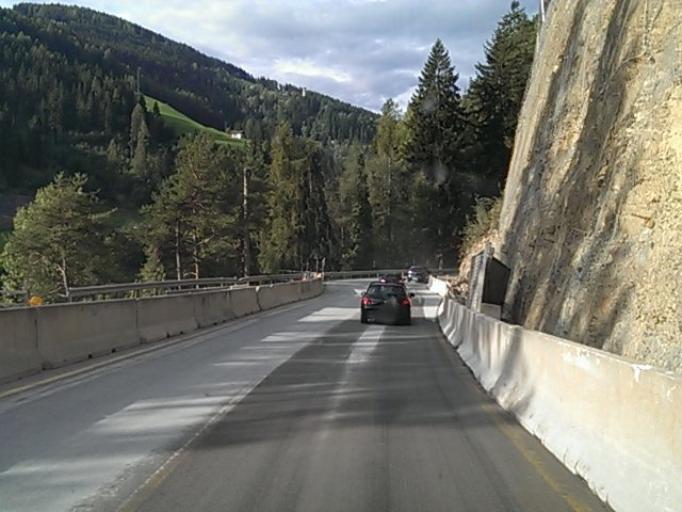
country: IT
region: Trentino-Alto Adige
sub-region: Bolzano
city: San Pancrazio
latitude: 46.5692
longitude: 11.0639
